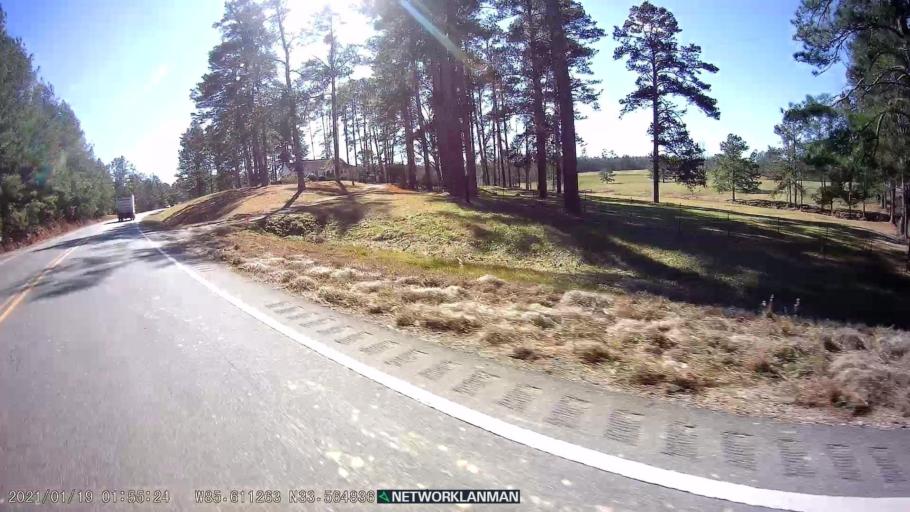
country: US
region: Alabama
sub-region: Cleburne County
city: Heflin
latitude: 33.5645
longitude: -85.6110
